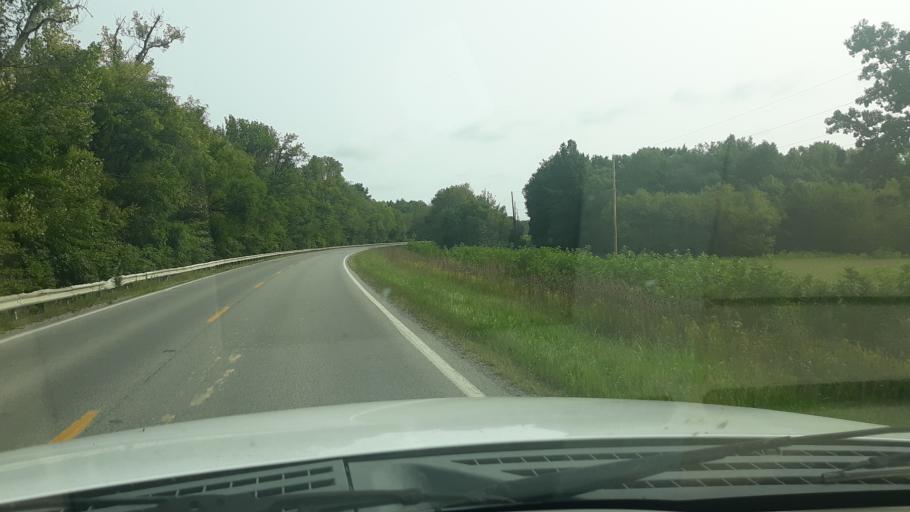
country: US
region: Illinois
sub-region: Saline County
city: Eldorado
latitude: 37.8913
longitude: -88.3825
